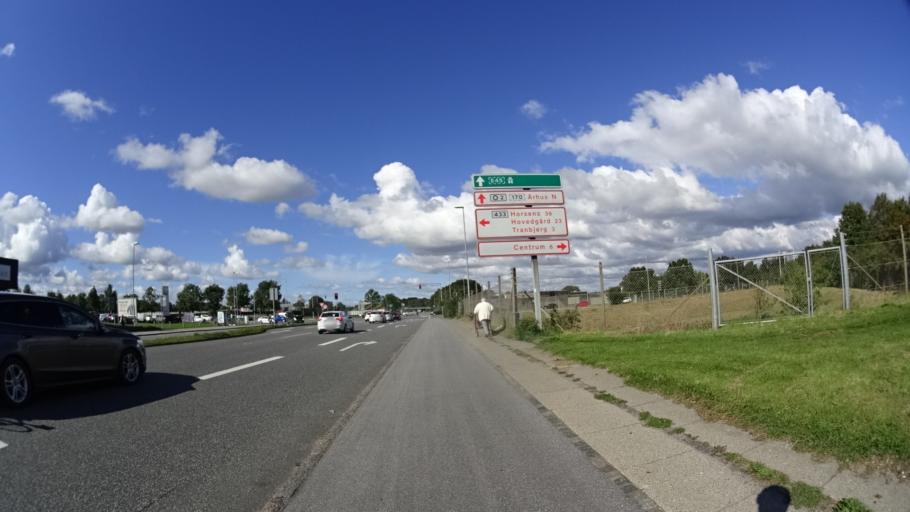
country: DK
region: Central Jutland
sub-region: Arhus Kommune
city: Stavtrup
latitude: 56.1121
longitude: 10.1581
